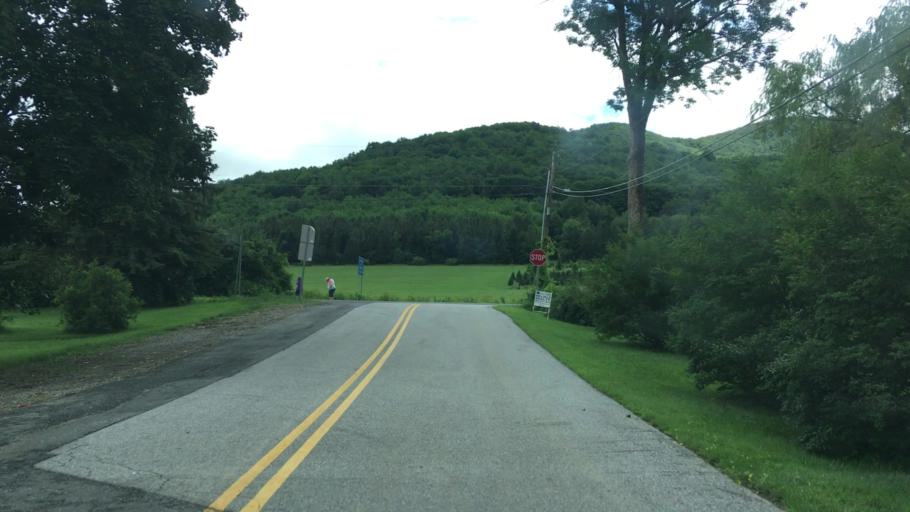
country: US
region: Vermont
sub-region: Bennington County
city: Bennington
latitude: 42.8826
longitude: -73.2264
